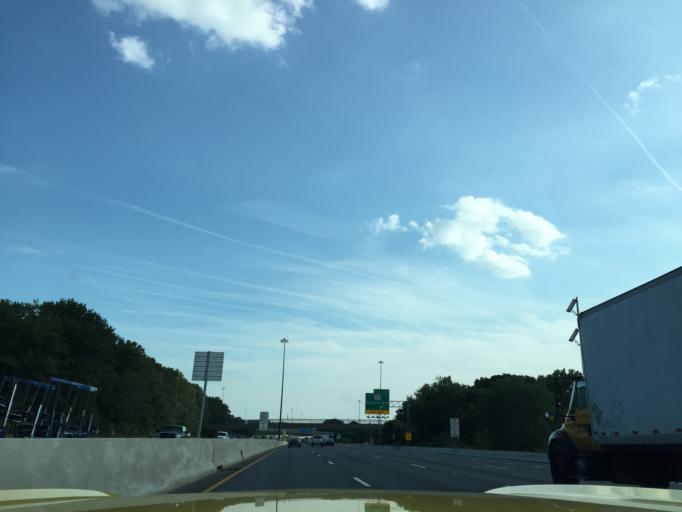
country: US
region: Maryland
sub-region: Baltimore County
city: Rosedale
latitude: 39.2939
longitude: -76.5321
